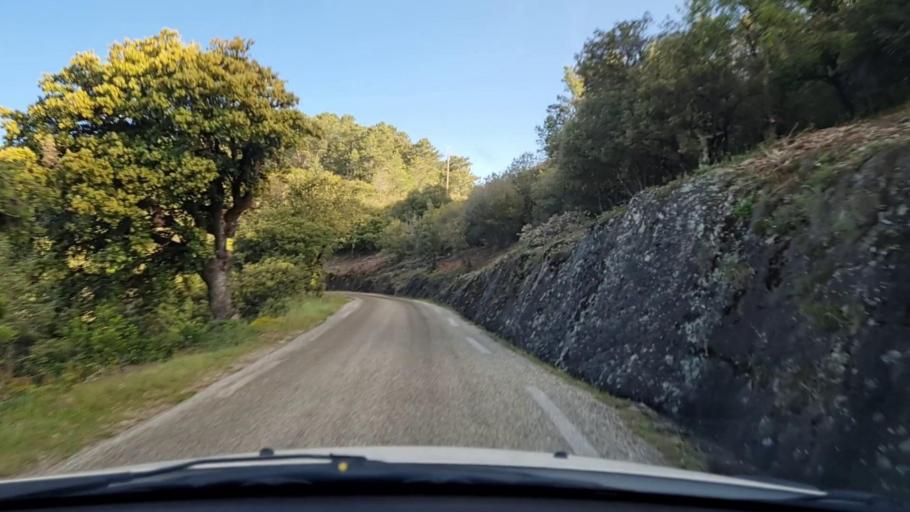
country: FR
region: Languedoc-Roussillon
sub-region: Departement du Gard
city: Branoux-les-Taillades
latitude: 44.1856
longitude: 3.9874
